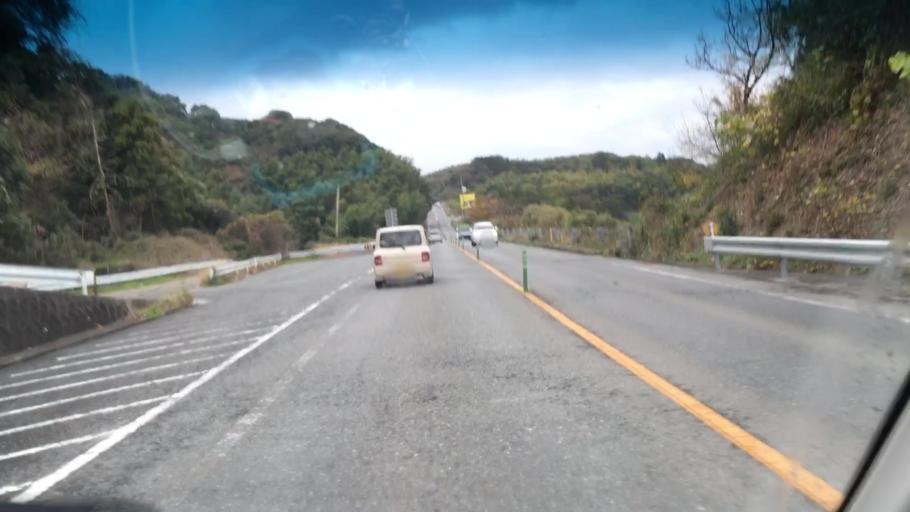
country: JP
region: Fukuoka
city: Maebaru-chuo
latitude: 33.5042
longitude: 130.1060
